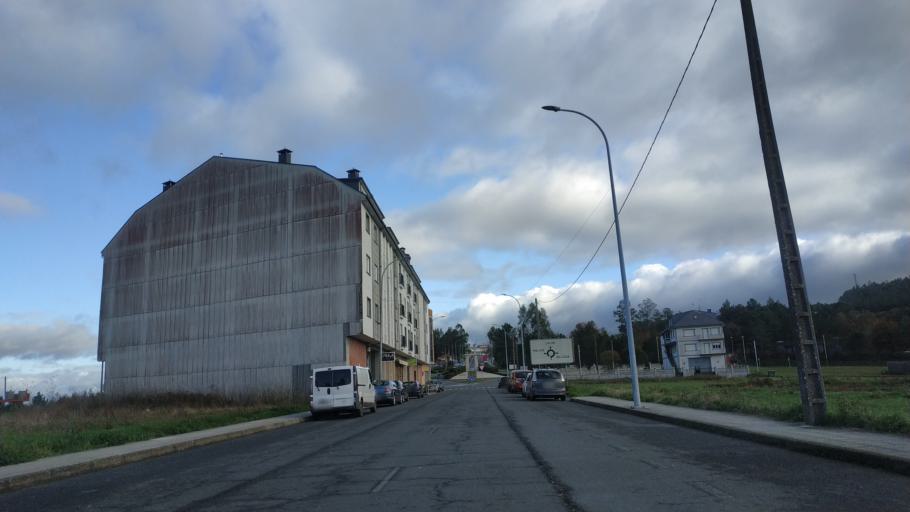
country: ES
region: Galicia
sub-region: Provincia de Pontevedra
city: Silleda
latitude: 42.7928
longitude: -8.1630
